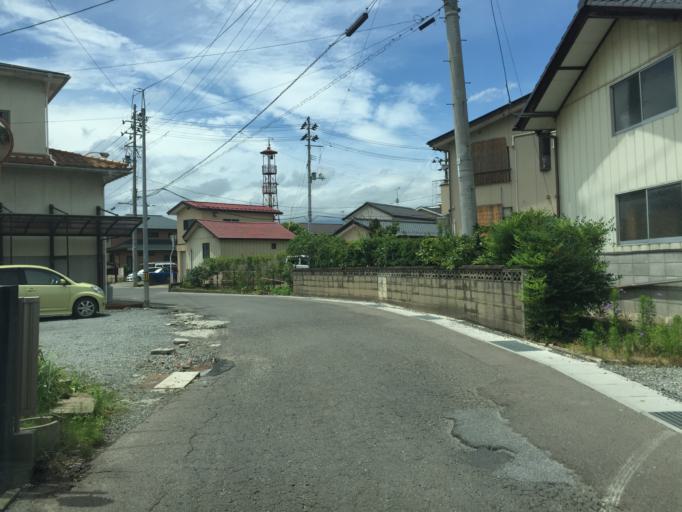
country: JP
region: Fukushima
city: Fukushima-shi
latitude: 37.7179
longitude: 140.4539
